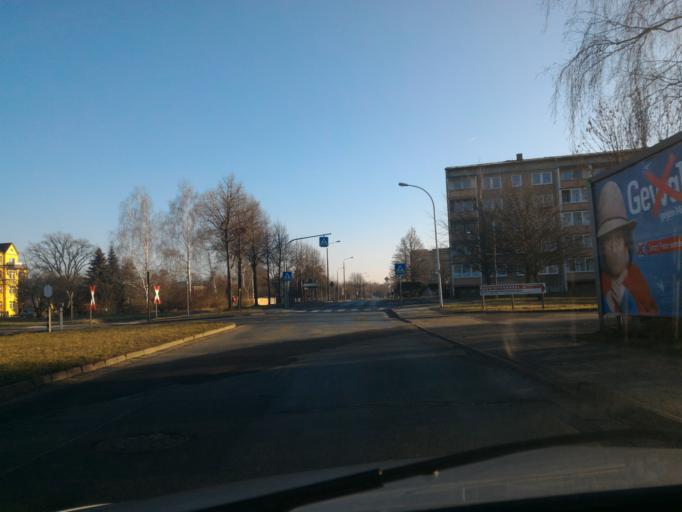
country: DE
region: Saxony
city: Zittau
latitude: 50.8904
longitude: 14.8159
